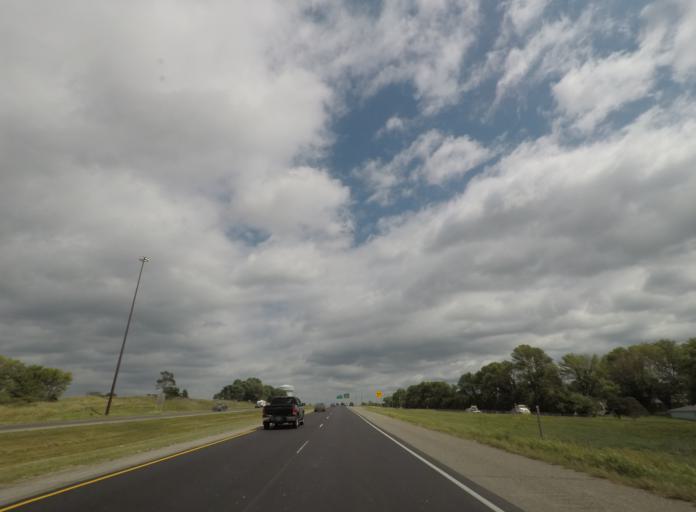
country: US
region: Iowa
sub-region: Linn County
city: Cedar Rapids
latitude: 41.9267
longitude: -91.6530
